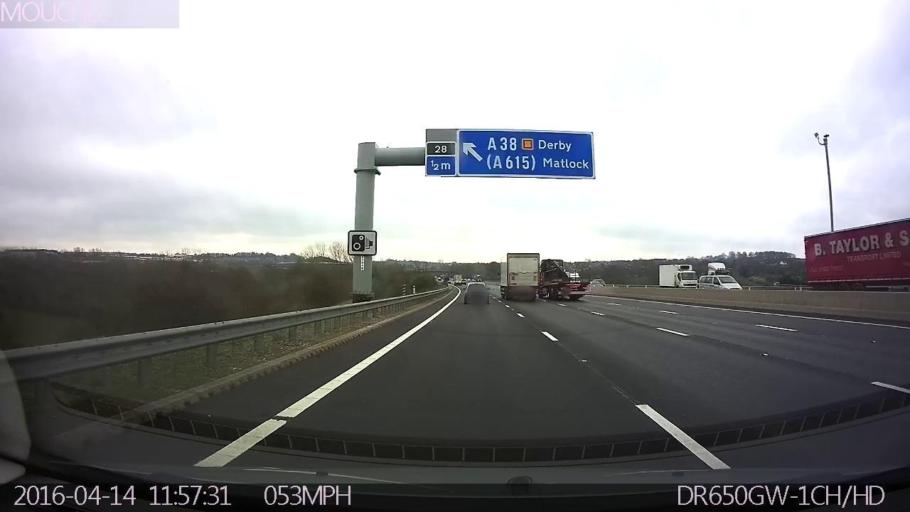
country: GB
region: England
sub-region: Derbyshire
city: Blackwell
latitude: 53.1162
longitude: -1.3339
